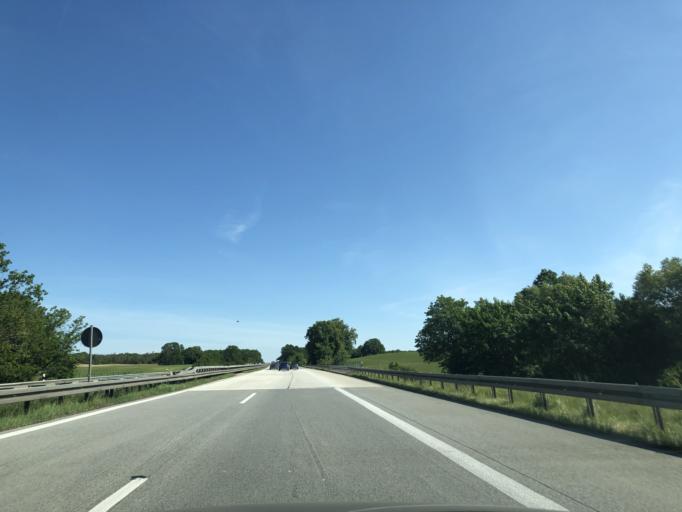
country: DE
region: Brandenburg
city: Althuttendorf
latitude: 52.9794
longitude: 13.8191
